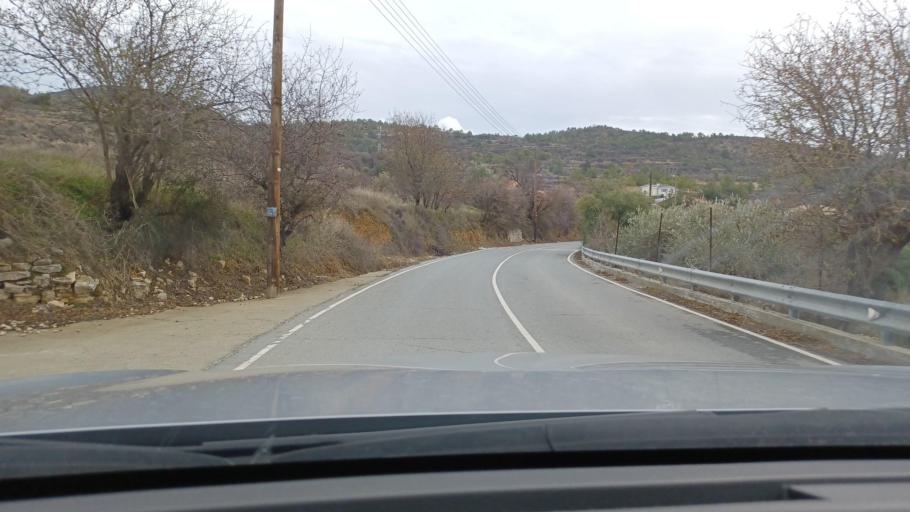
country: CY
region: Limassol
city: Pelendri
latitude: 34.8080
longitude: 32.9134
